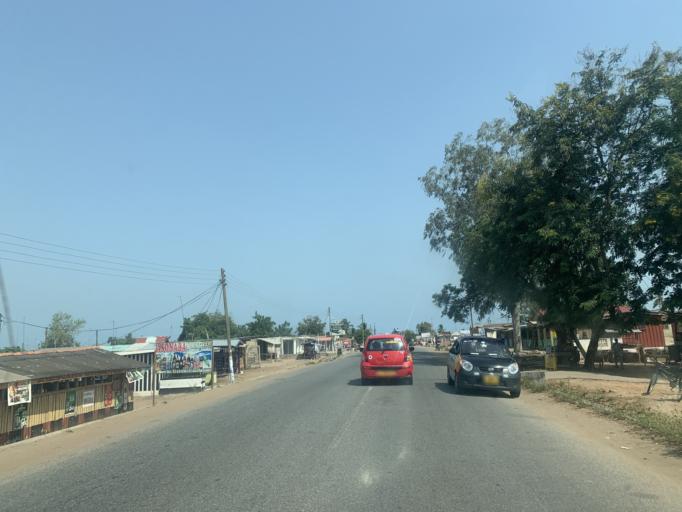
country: GH
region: Central
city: Winneba
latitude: 5.3944
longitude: -0.6479
